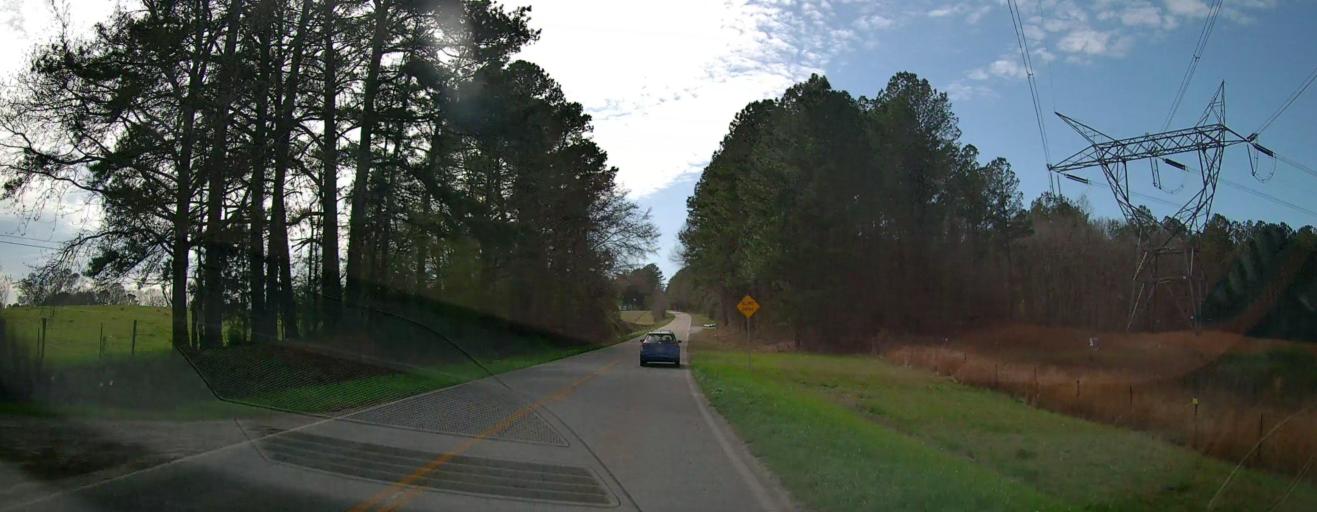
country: US
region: Georgia
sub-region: Monroe County
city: Forsyth
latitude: 33.0579
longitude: -83.8733
